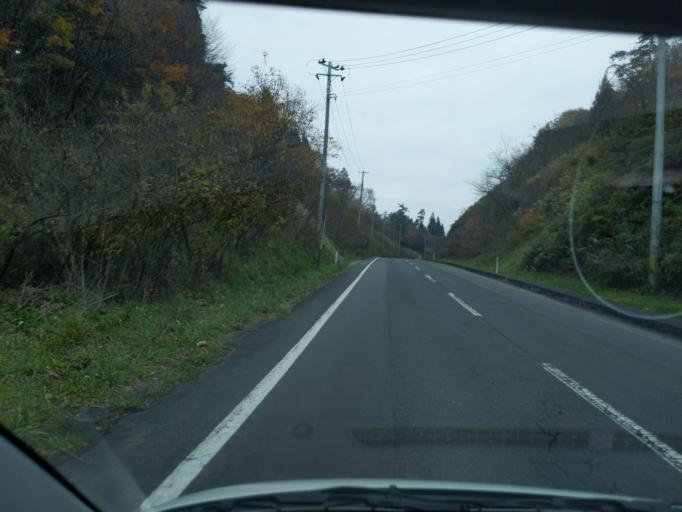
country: JP
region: Iwate
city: Mizusawa
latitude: 39.1645
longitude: 141.2039
